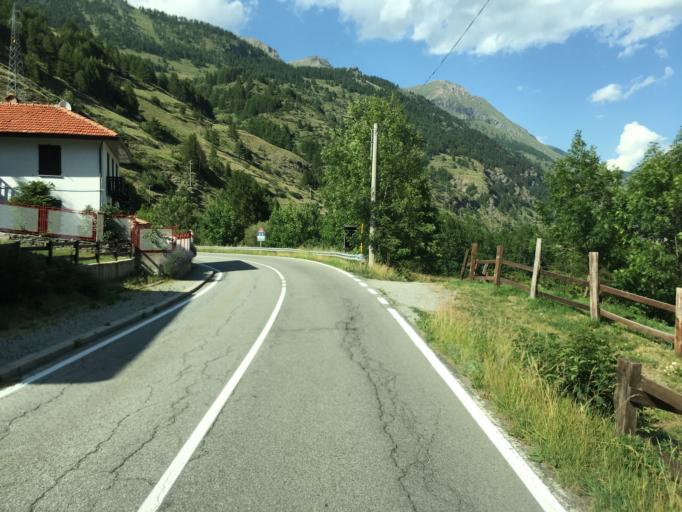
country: IT
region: Piedmont
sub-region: Provincia di Torino
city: Pragelato-Rua
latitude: 45.0336
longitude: 6.9652
